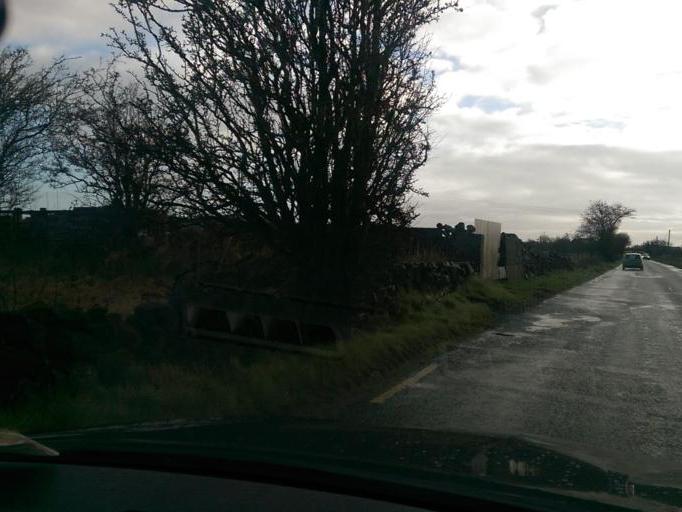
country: IE
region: Connaught
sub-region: County Galway
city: Oranmore
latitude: 53.3146
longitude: -8.8765
